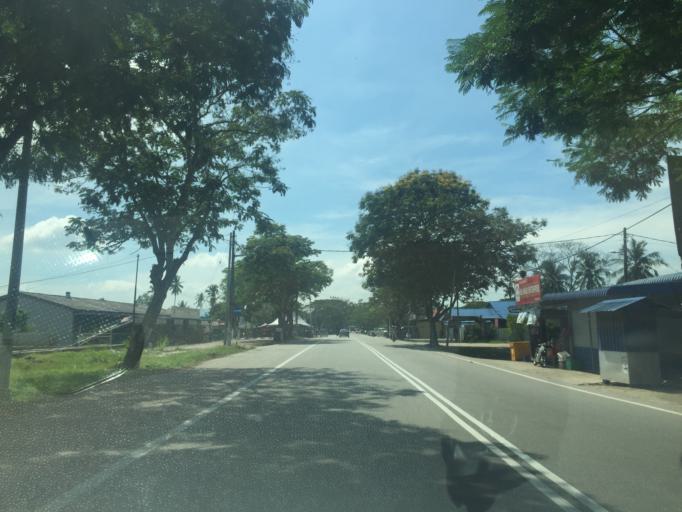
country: MY
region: Penang
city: Tasek Glugor
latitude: 5.4873
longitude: 100.4575
